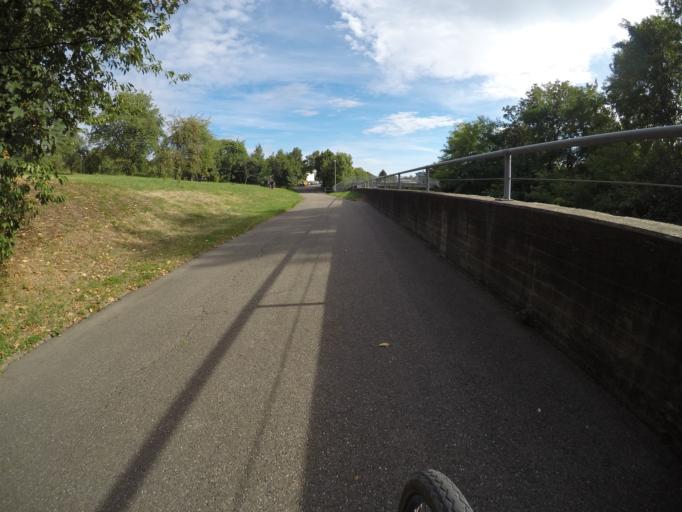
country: DE
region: Baden-Wuerttemberg
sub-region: Regierungsbezirk Stuttgart
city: Marbach am Neckar
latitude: 48.9070
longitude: 9.2604
